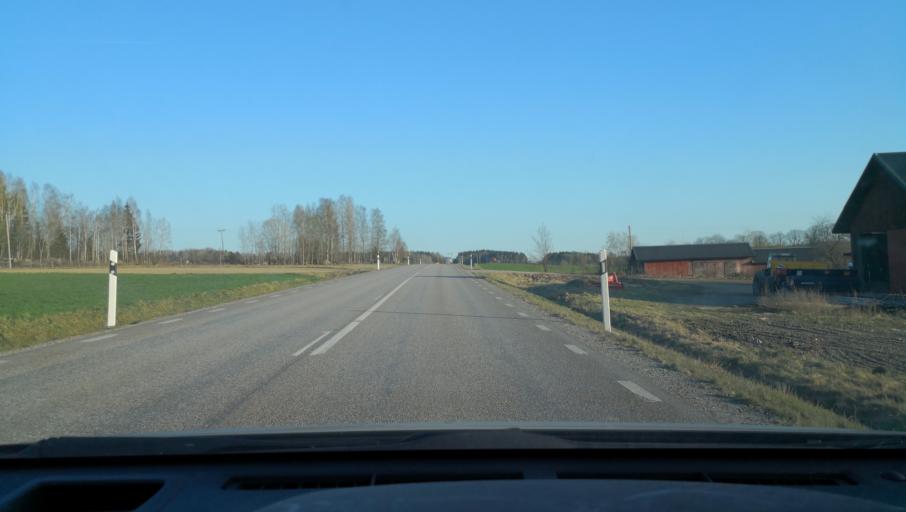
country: SE
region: Uppsala
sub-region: Heby Kommun
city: Heby
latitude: 59.9253
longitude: 16.8786
